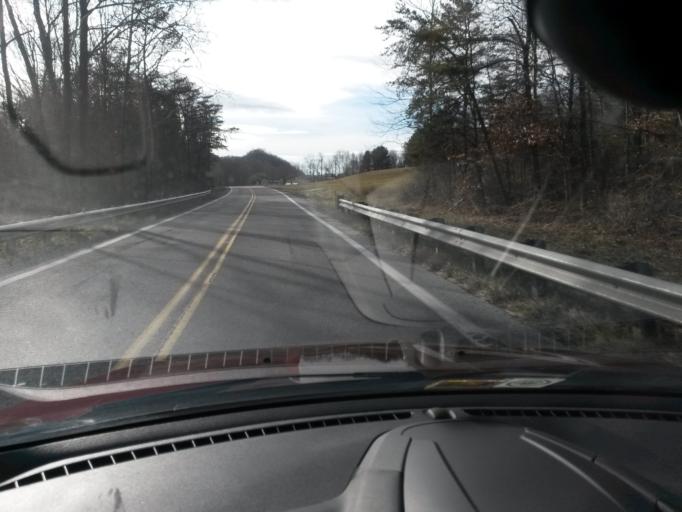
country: US
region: Virginia
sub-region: Augusta County
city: Jolivue
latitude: 38.1150
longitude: -79.2945
